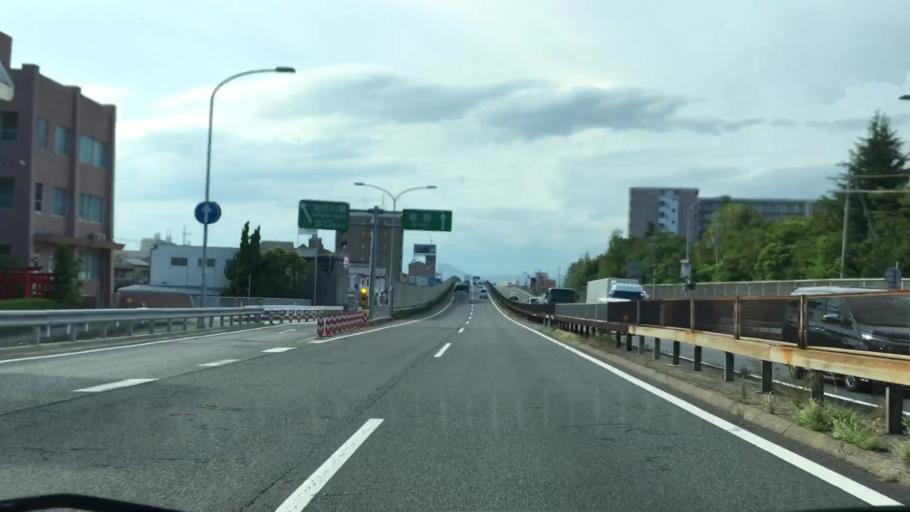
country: JP
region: Hyogo
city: Kakogawacho-honmachi
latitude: 34.7470
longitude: 134.8712
